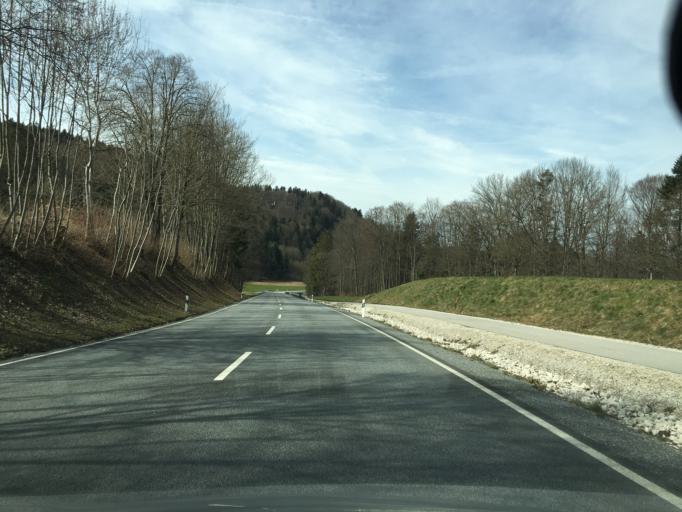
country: DE
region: Bavaria
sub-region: Upper Bavaria
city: Siegsdorf
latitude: 47.8091
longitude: 12.6900
